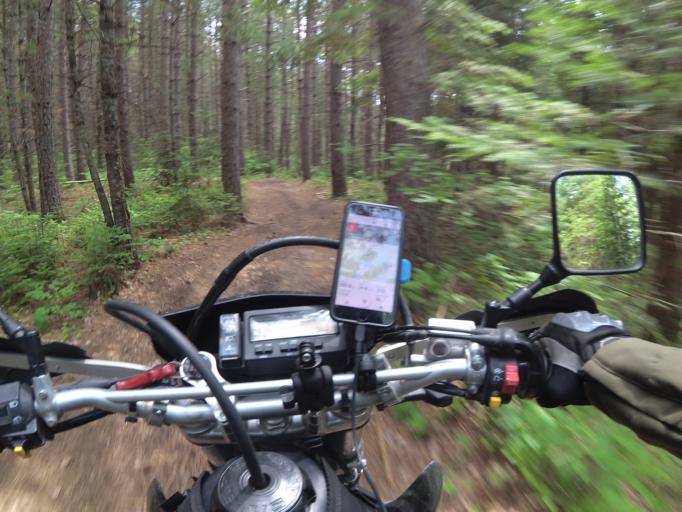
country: CA
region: Ontario
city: Bancroft
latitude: 45.0225
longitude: -77.2645
